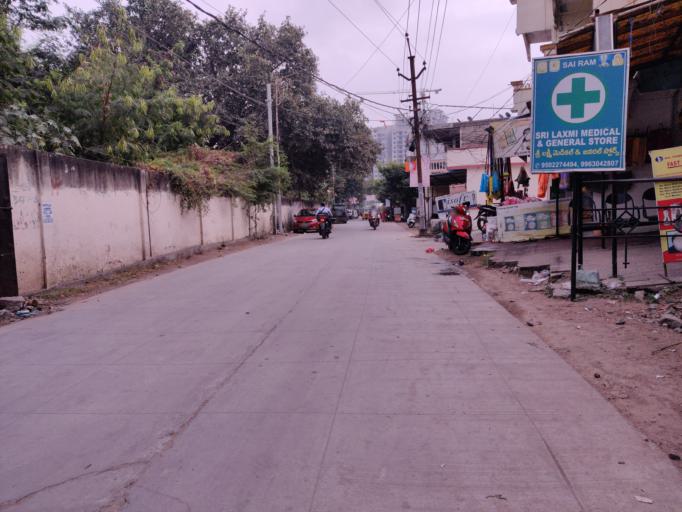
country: IN
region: Telangana
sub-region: Hyderabad
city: Hyderabad
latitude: 17.4065
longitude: 78.4015
